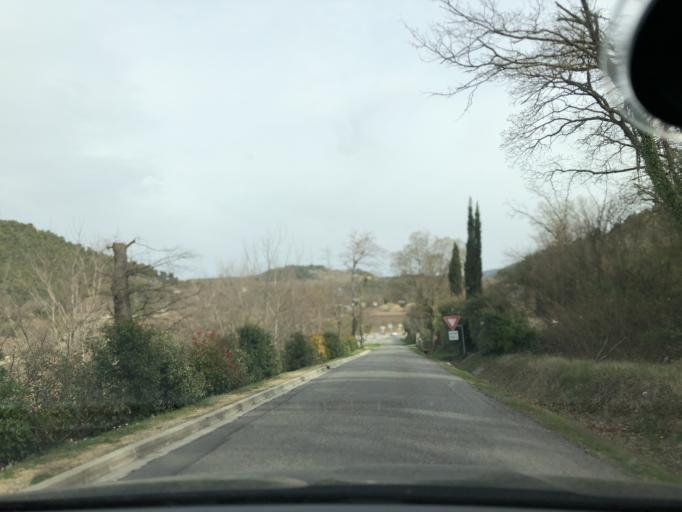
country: FR
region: Provence-Alpes-Cote d'Azur
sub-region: Departement du Vaucluse
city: Menerbes
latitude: 43.8316
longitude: 5.2126
